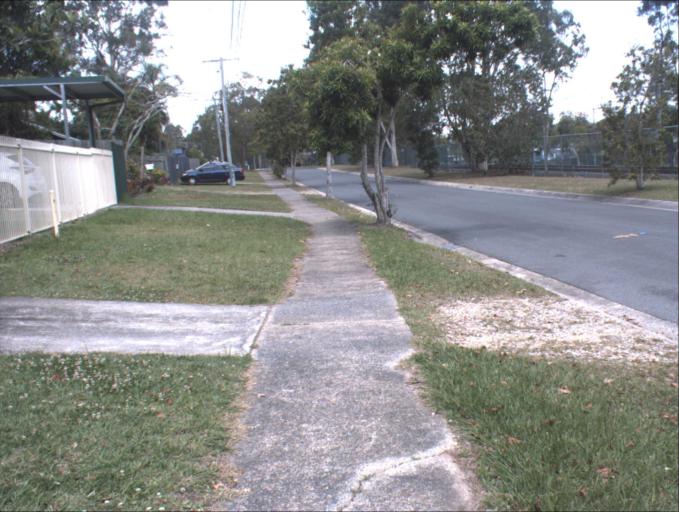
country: AU
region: Queensland
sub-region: Logan
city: Woodridge
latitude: -27.6225
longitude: 153.0979
